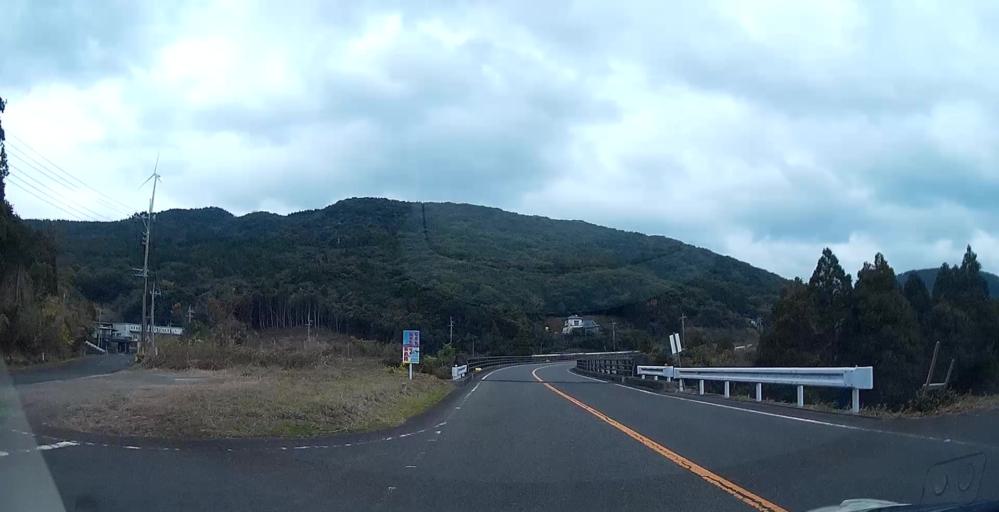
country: JP
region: Kagoshima
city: Akune
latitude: 32.1051
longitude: 130.1499
